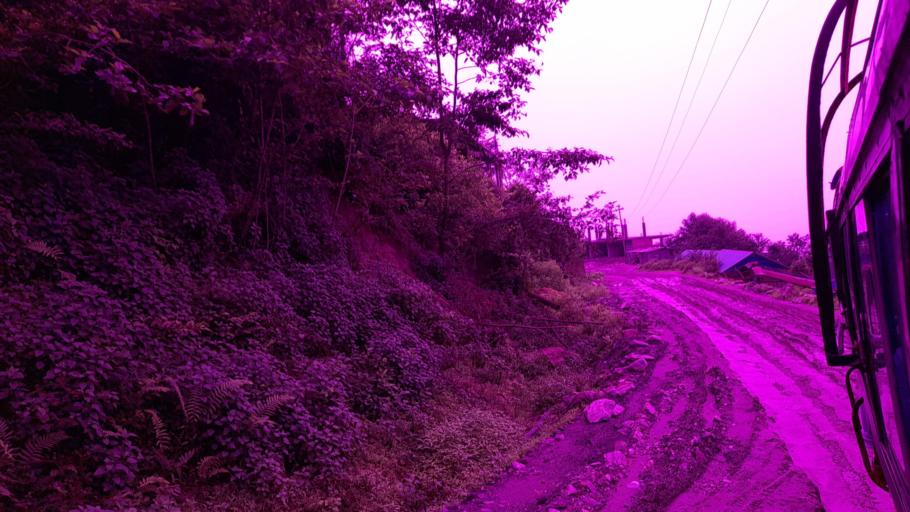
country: NP
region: Central Region
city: Kirtipur
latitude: 27.8144
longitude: 85.2204
